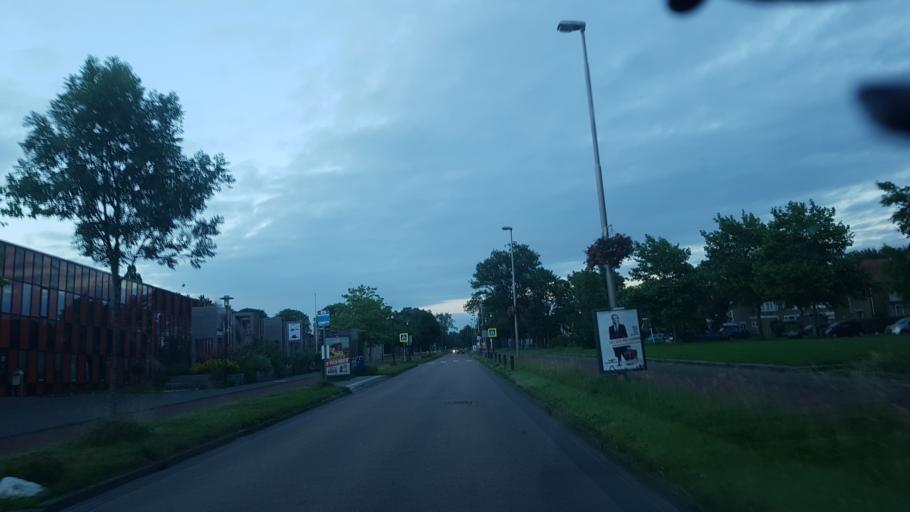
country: NL
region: Friesland
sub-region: Gemeente Leeuwarden
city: Leeuwarden
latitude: 53.2083
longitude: 5.8208
